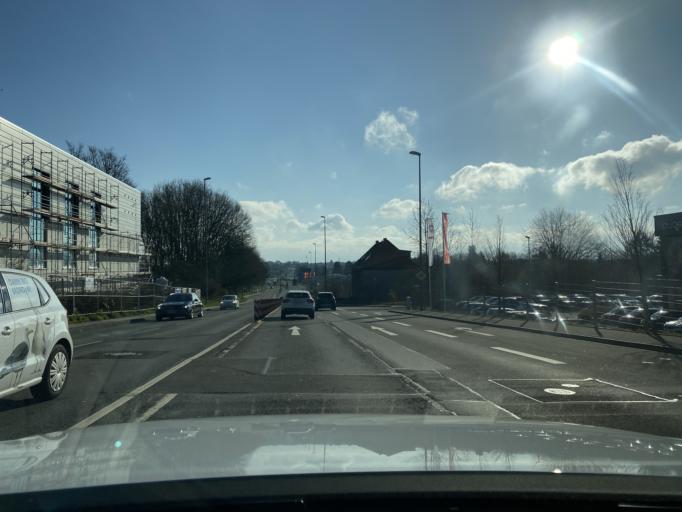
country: DE
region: North Rhine-Westphalia
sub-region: Regierungsbezirk Dusseldorf
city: Remscheid
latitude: 51.1802
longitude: 7.2279
